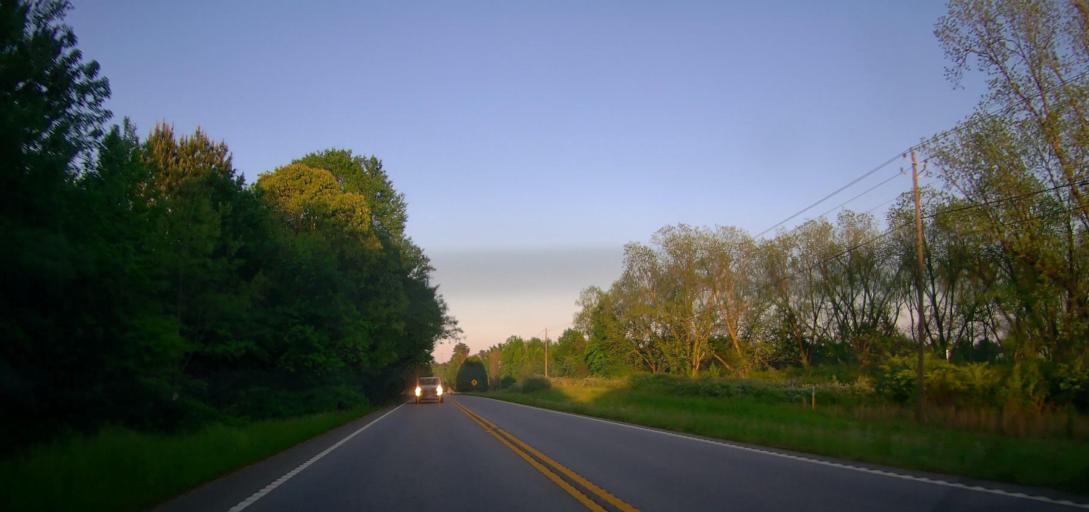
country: US
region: Georgia
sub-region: Newton County
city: Oakwood
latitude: 33.4408
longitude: -84.0053
